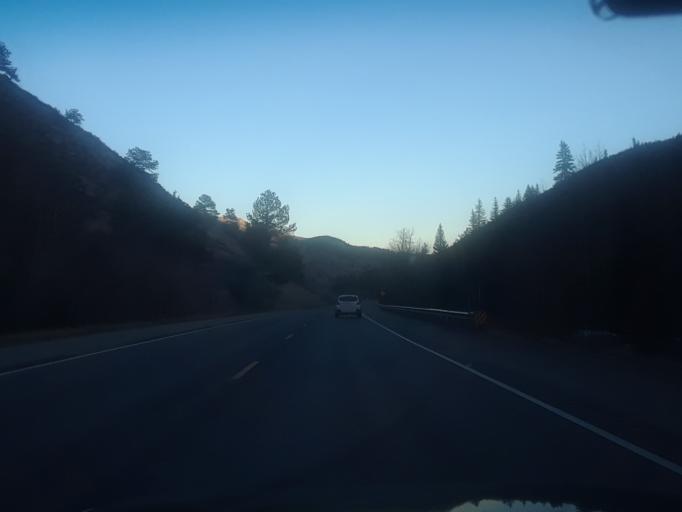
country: US
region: Colorado
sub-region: Clear Creek County
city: Georgetown
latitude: 39.4599
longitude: -105.6958
